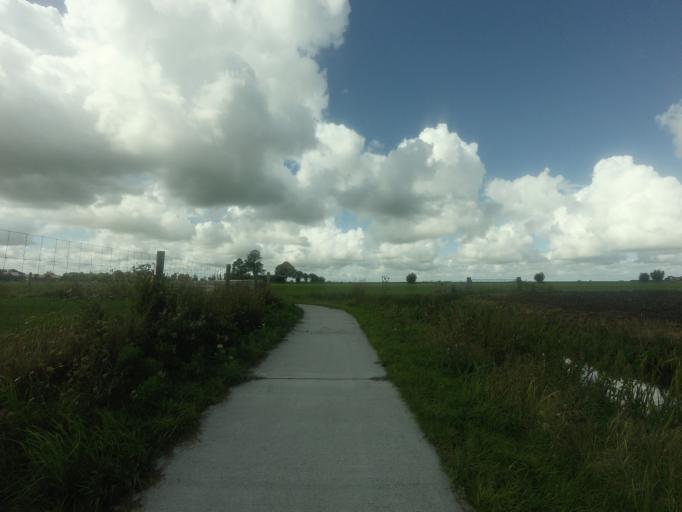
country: NL
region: Friesland
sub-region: Gemeente Littenseradiel
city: Makkum
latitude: 53.0906
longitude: 5.7072
